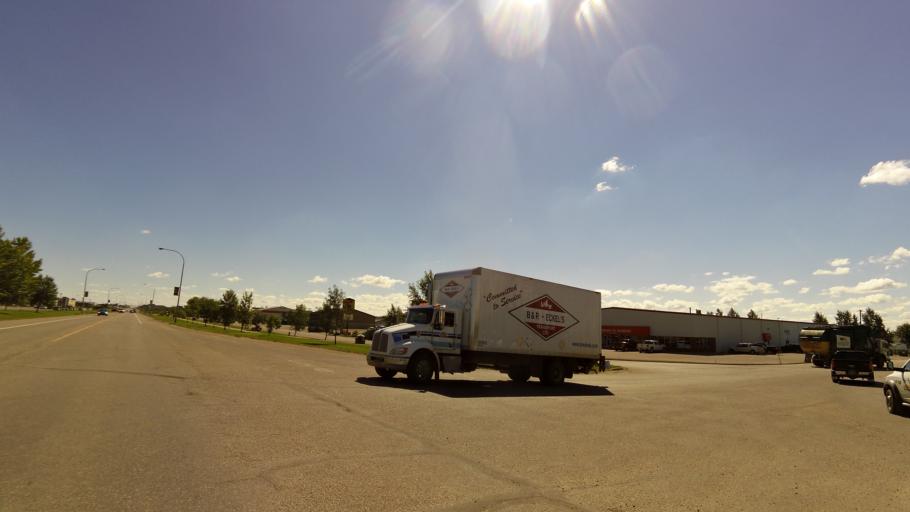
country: CA
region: Alberta
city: Wainwright
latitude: 52.8434
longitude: -110.8450
